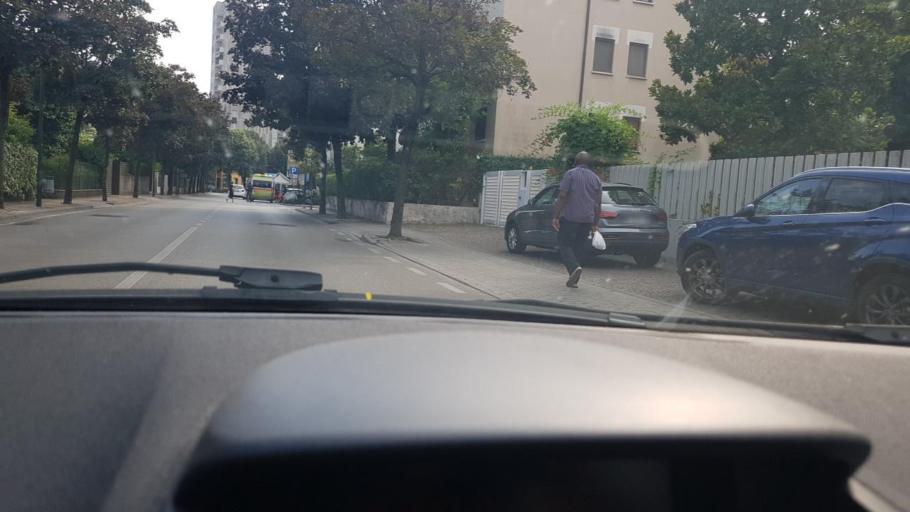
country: IT
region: Friuli Venezia Giulia
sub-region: Provincia di Pordenone
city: Pordenone
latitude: 45.9607
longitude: 12.6663
